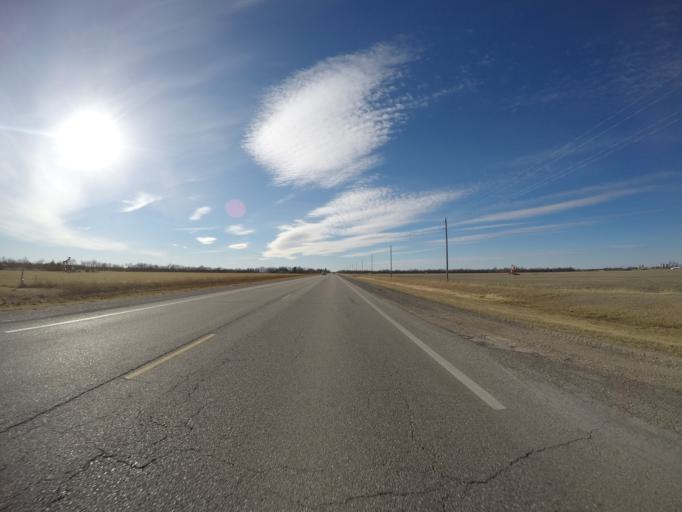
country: US
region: Kansas
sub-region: McPherson County
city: Moundridge
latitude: 38.3770
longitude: -97.4823
